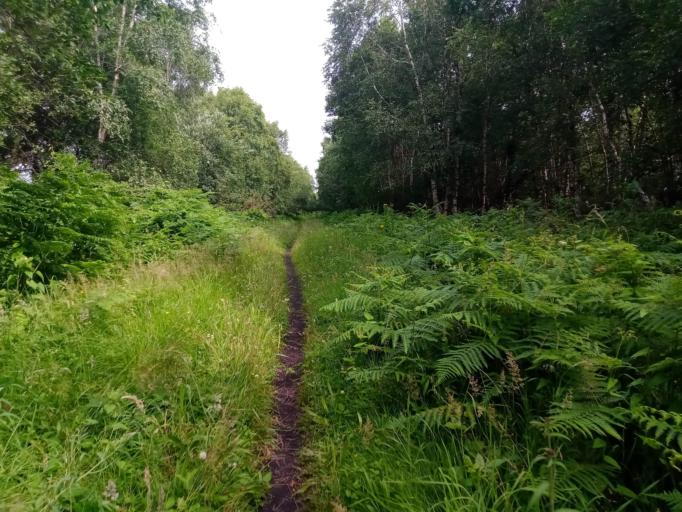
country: IE
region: Leinster
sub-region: Laois
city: Abbeyleix
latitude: 52.8851
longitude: -7.3504
